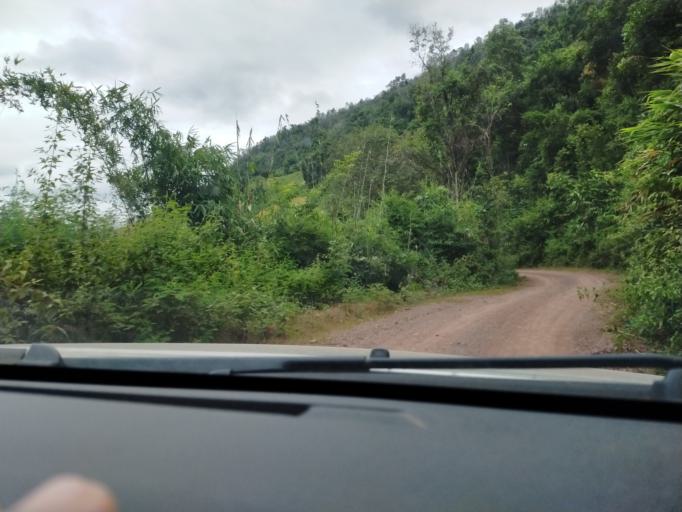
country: TH
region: Nan
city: Chaloem Phra Kiat
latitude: 19.7873
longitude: 101.3600
